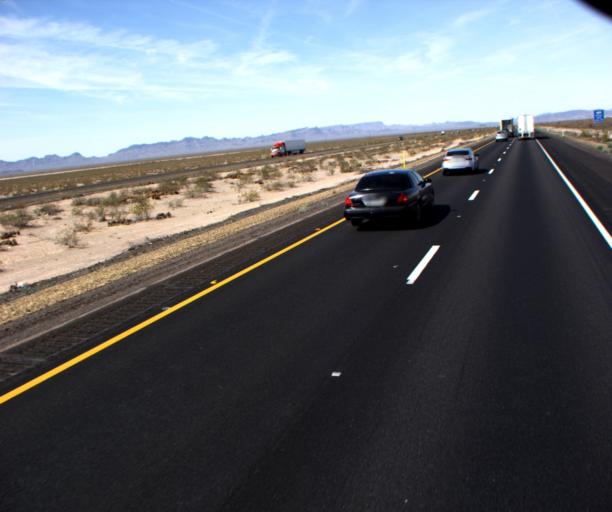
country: US
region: Arizona
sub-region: La Paz County
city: Salome
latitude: 33.6195
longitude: -113.6878
